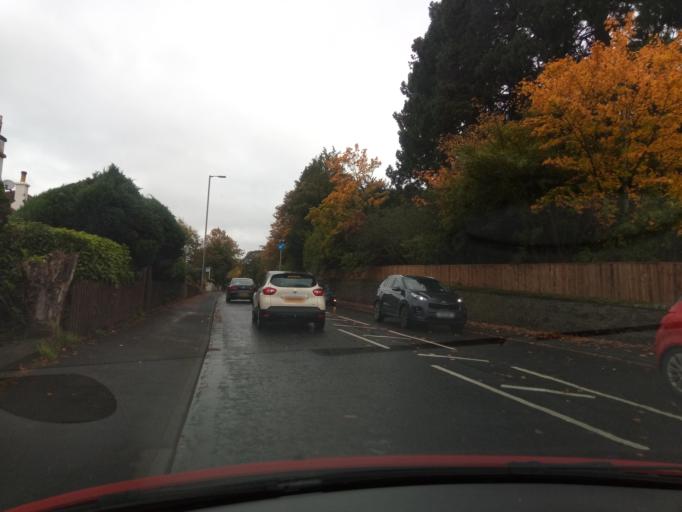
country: GB
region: Scotland
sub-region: The Scottish Borders
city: Galashiels
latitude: 55.6084
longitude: -2.7965
